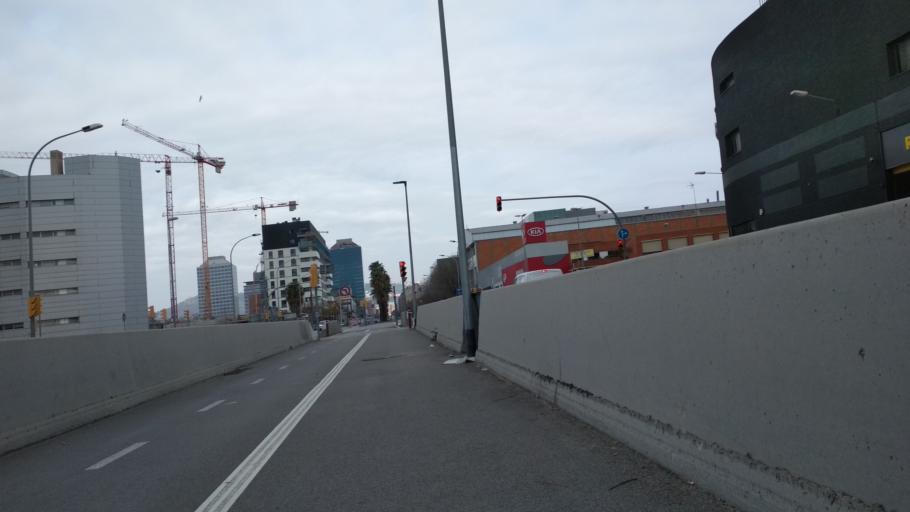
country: ES
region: Catalonia
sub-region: Provincia de Barcelona
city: Sants-Montjuic
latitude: 41.3505
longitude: 2.1461
